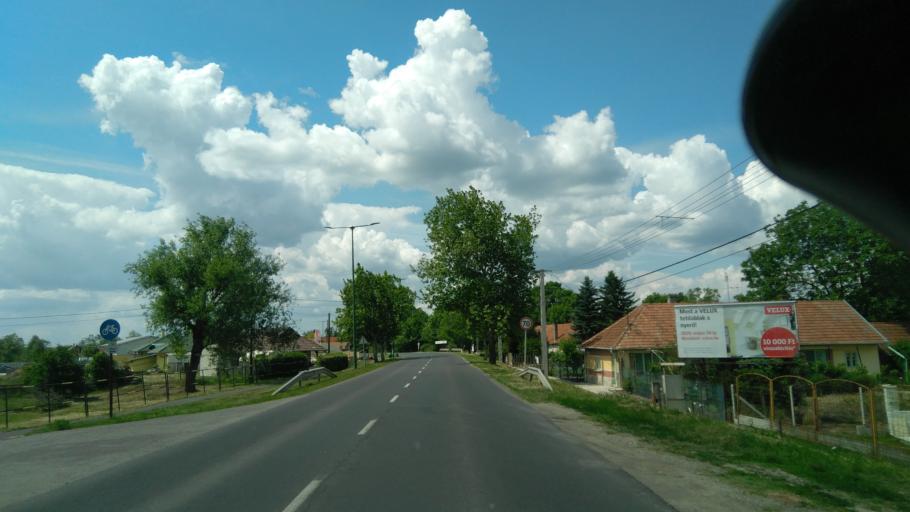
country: HU
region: Bekes
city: Gyula
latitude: 46.6510
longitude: 21.2469
